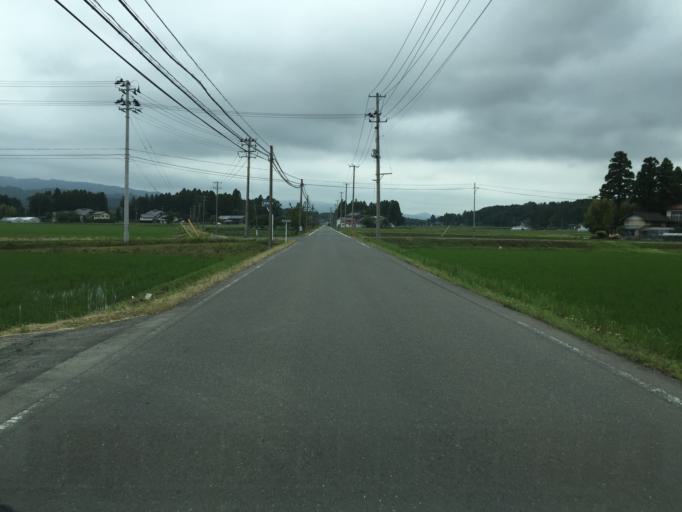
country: JP
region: Miyagi
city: Marumori
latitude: 37.7277
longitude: 140.9347
